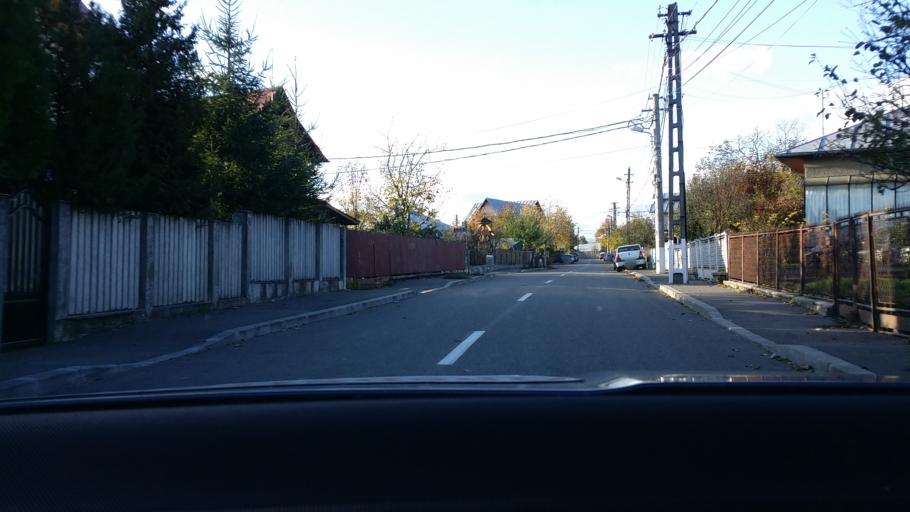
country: RO
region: Prahova
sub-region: Municipiul Campina
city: Campina
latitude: 45.1403
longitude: 25.7391
